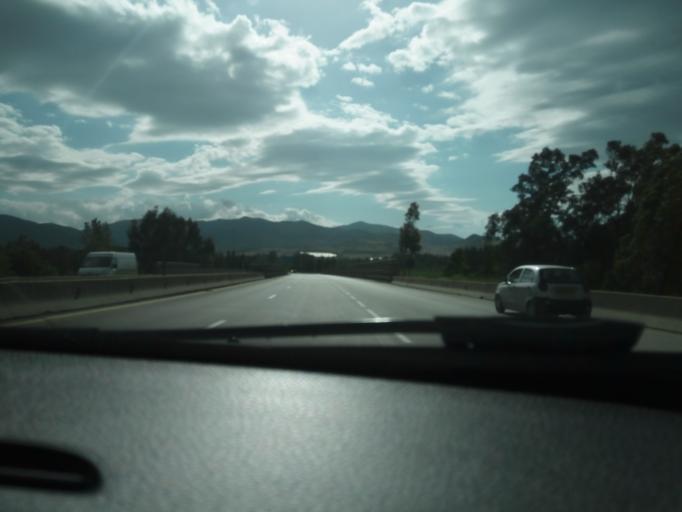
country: DZ
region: Tipaza
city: El Affroun
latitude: 36.4473
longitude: 2.5953
